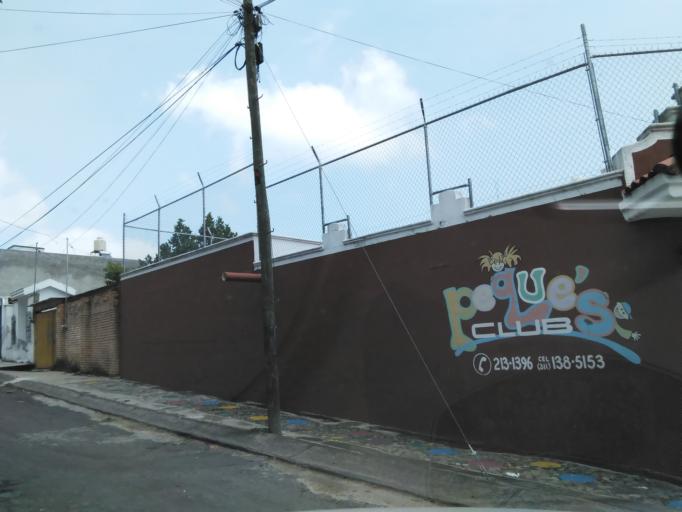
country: MX
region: Nayarit
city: Tepic
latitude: 21.5159
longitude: -104.9191
